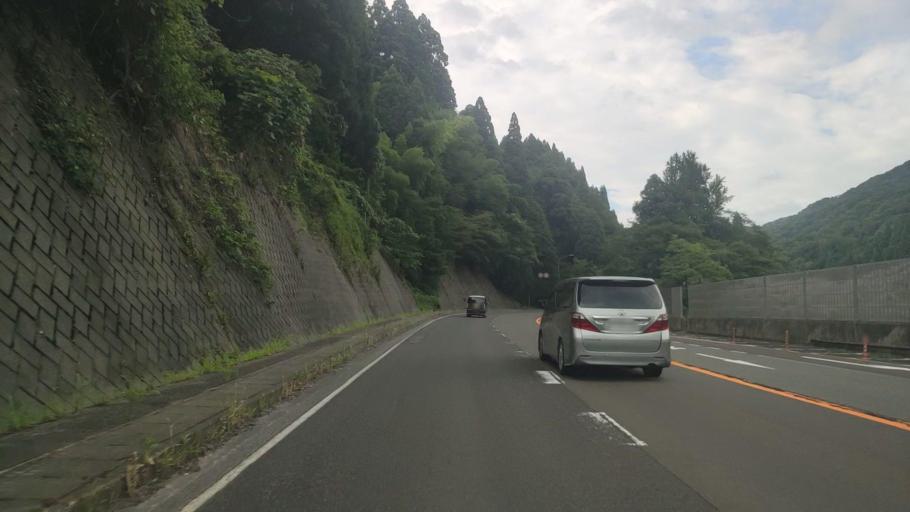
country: JP
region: Fukui
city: Takefu
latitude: 35.8336
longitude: 136.1193
